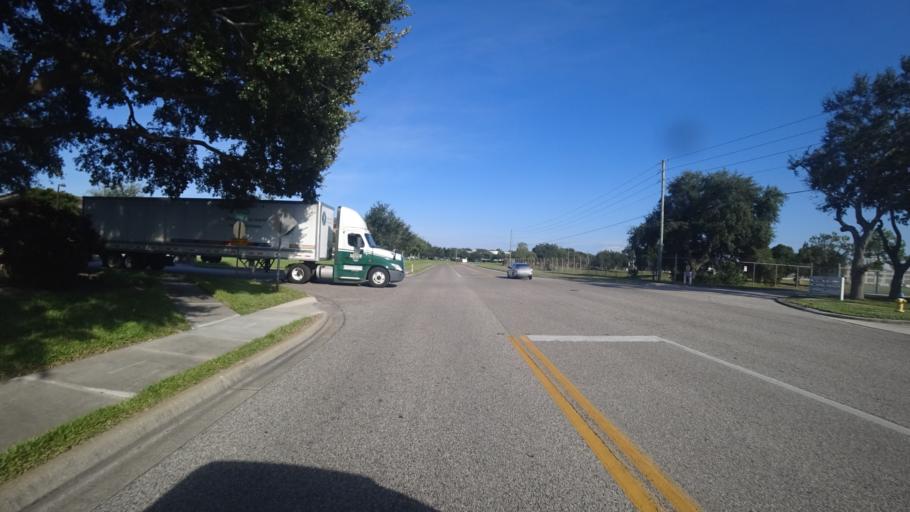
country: US
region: Florida
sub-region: Manatee County
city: Whitfield
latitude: 27.4077
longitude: -82.5598
